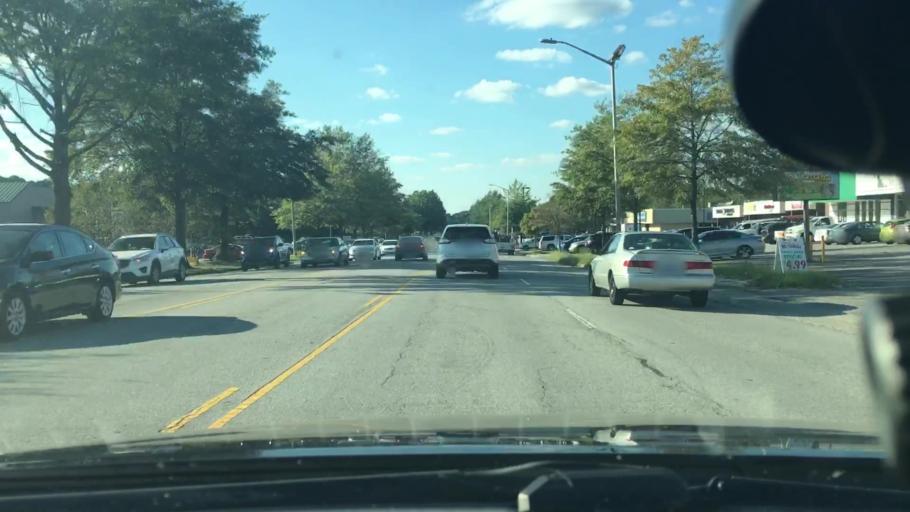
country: US
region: North Carolina
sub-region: Pitt County
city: Greenville
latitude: 35.5863
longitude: -77.3714
